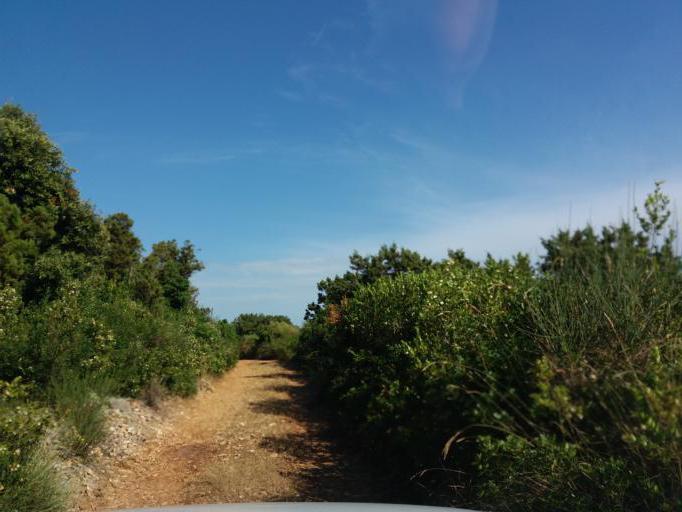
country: HR
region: Zadarska
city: Ugljan
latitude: 44.1270
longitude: 14.8680
